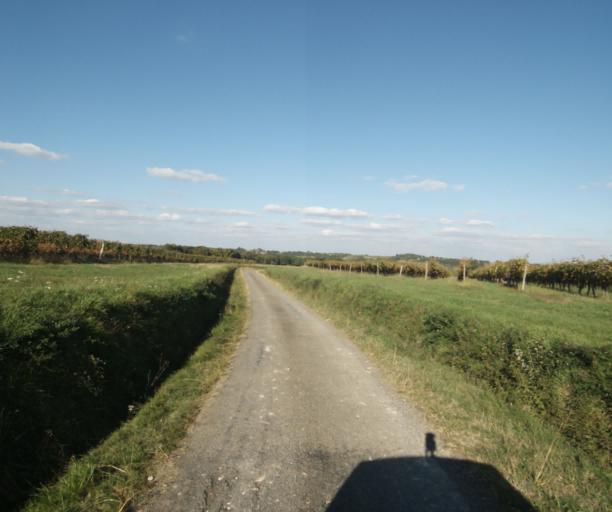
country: FR
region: Midi-Pyrenees
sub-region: Departement du Gers
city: Eauze
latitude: 43.8121
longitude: 0.1398
